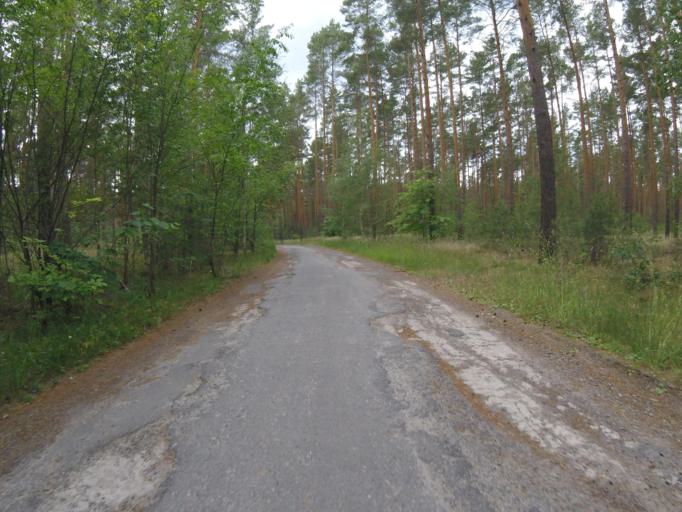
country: DE
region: Brandenburg
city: Gross Koris
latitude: 52.1854
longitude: 13.6887
